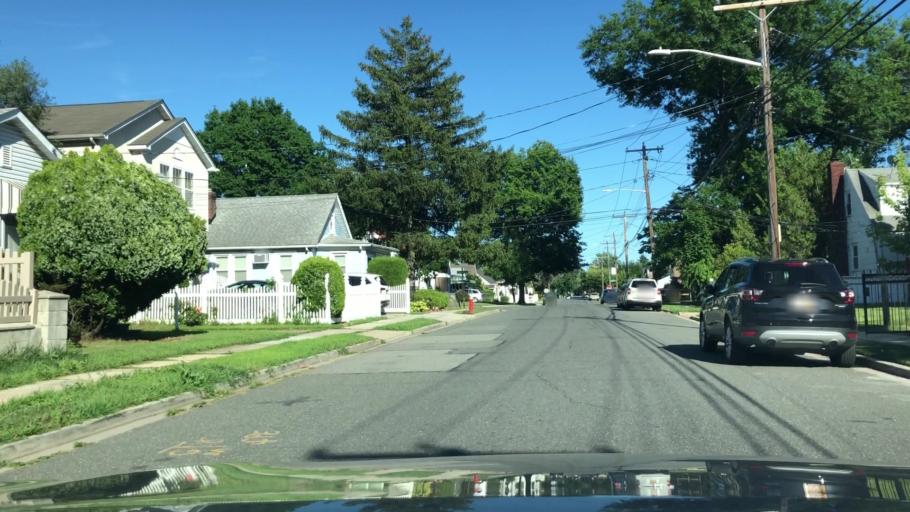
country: US
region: New York
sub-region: Nassau County
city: Elmont
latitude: 40.7053
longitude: -73.7049
